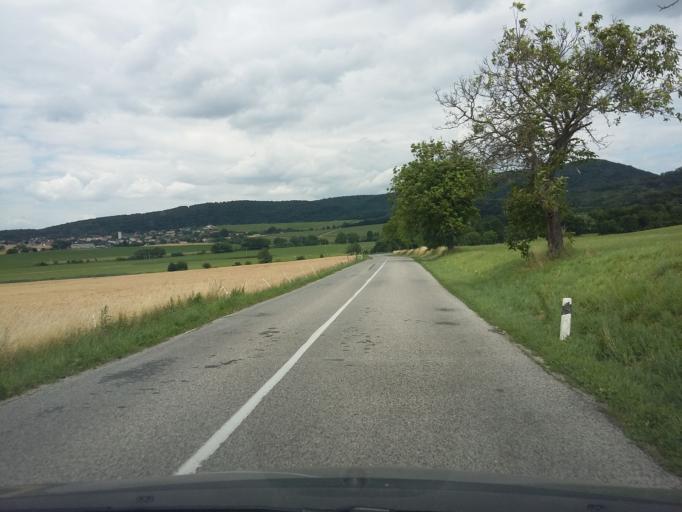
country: SK
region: Trnavsky
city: Smolenice
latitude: 48.5417
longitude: 17.3430
